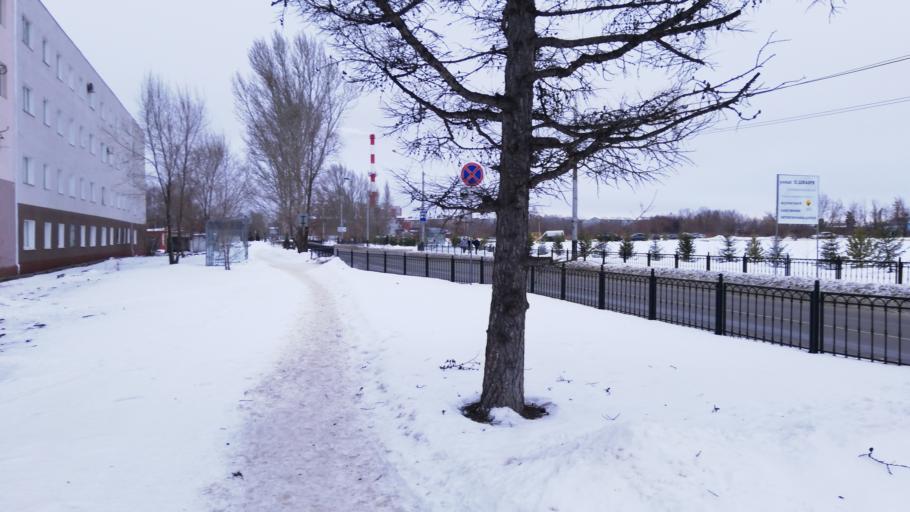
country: RU
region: Omsk
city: Omsk
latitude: 54.9573
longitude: 73.3179
